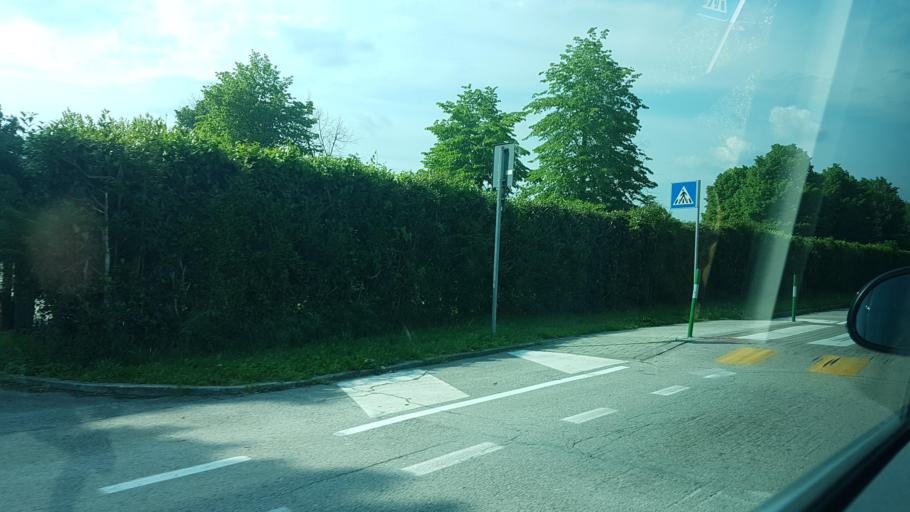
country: IT
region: Veneto
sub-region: Provincia di Padova
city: Noventa
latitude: 45.4246
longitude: 11.9367
